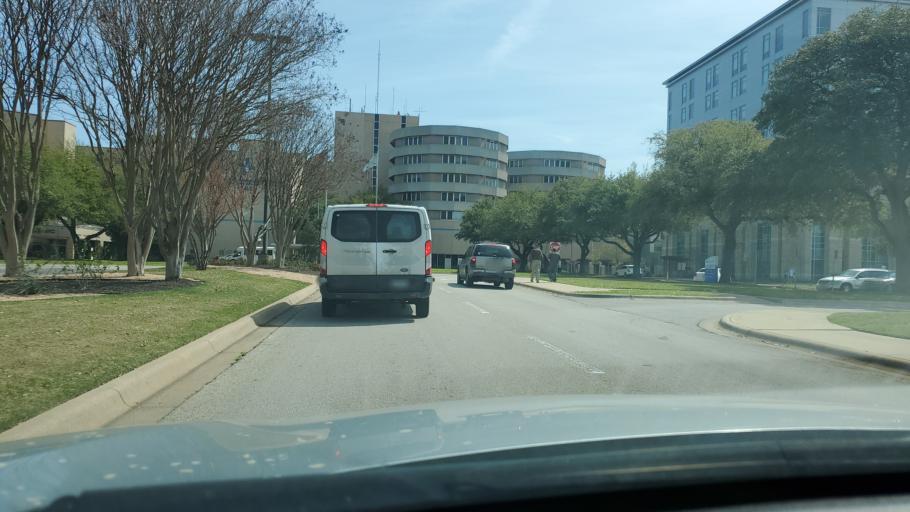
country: US
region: Texas
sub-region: Bell County
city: Temple
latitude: 31.0786
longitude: -97.3655
